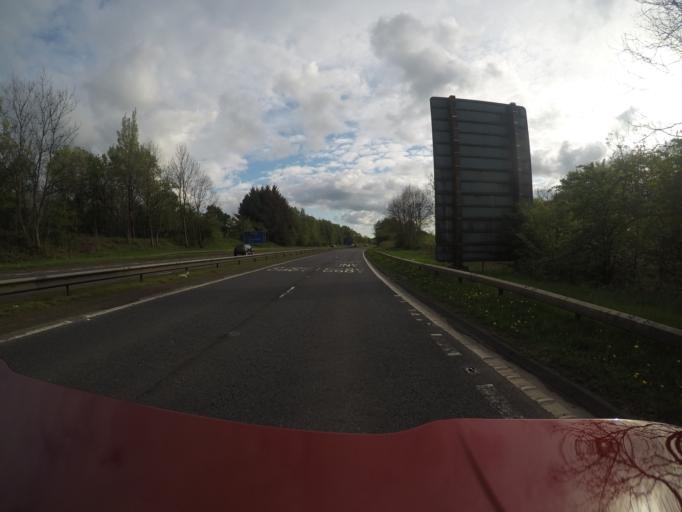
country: GB
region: Scotland
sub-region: Renfrewshire
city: Erskine
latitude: 55.9062
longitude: -4.4742
